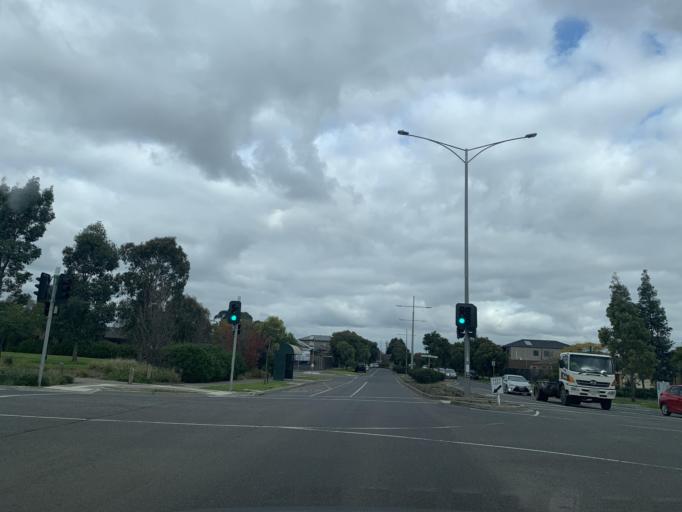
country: AU
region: Victoria
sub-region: Whittlesea
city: Epping
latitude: -37.6249
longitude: 145.0049
